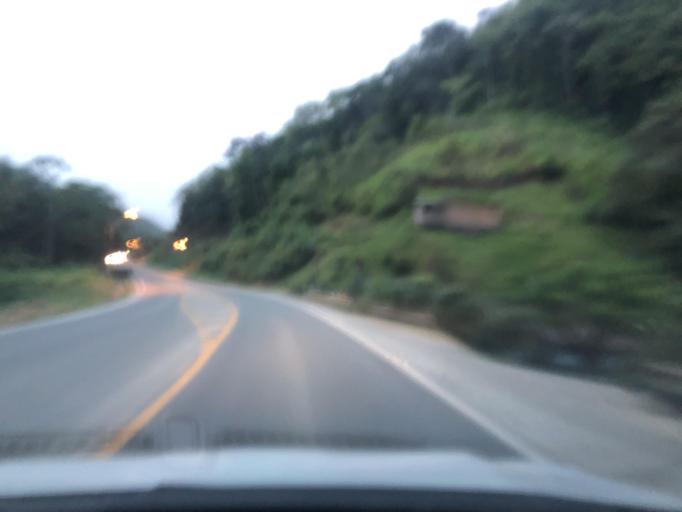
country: BR
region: Santa Catarina
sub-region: Pomerode
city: Pomerode
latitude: -26.7186
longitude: -49.0587
